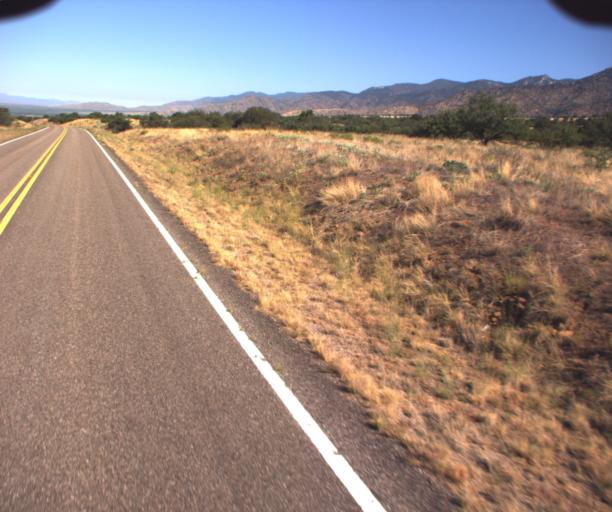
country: US
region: Arizona
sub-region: Graham County
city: Swift Trail Junction
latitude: 32.5991
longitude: -109.8764
